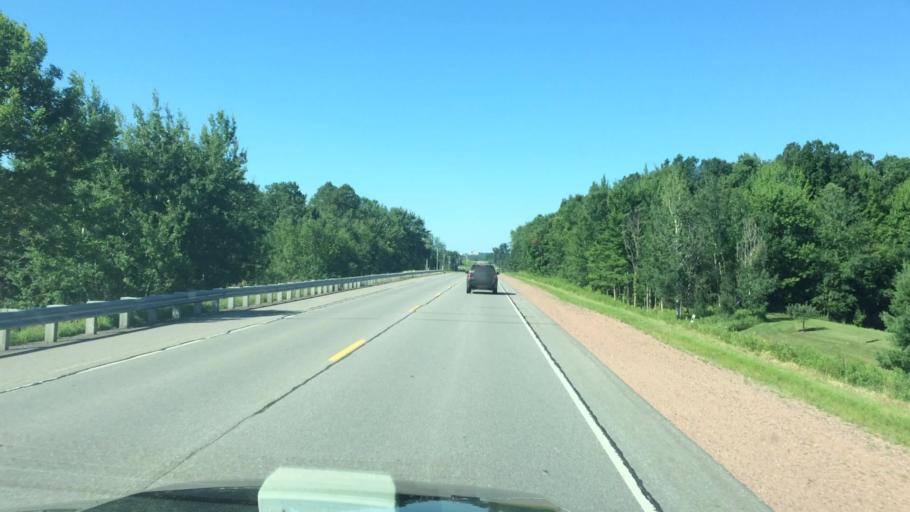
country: US
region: Wisconsin
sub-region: Wood County
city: Marshfield
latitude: 44.7158
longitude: -90.1107
